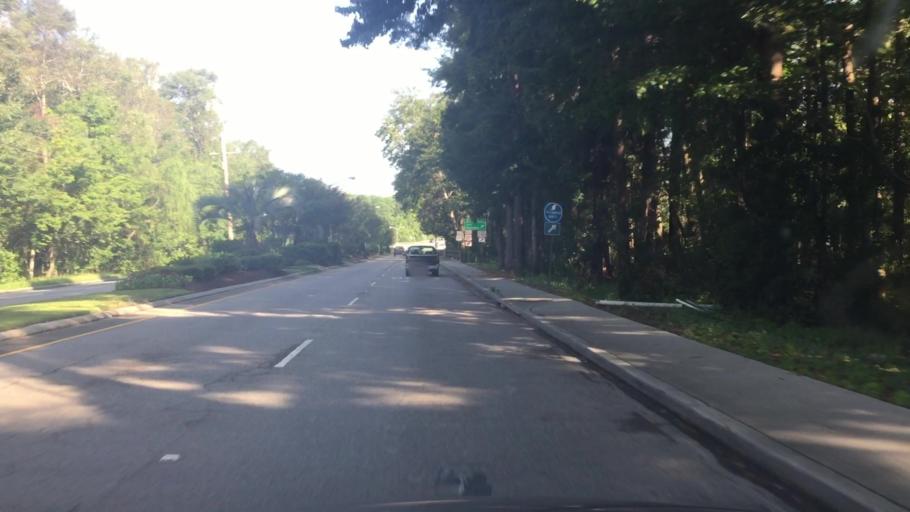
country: US
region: South Carolina
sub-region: Horry County
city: North Myrtle Beach
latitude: 33.8432
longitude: -78.6489
